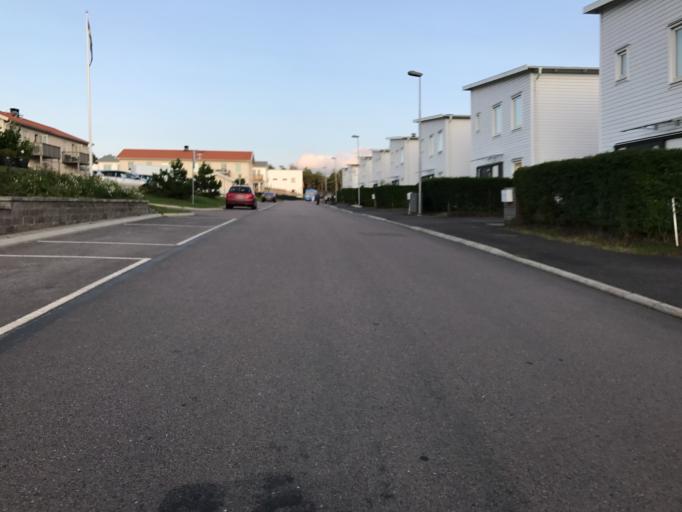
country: SE
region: Vaestra Goetaland
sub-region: Goteborg
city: Majorna
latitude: 57.7200
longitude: 11.8879
